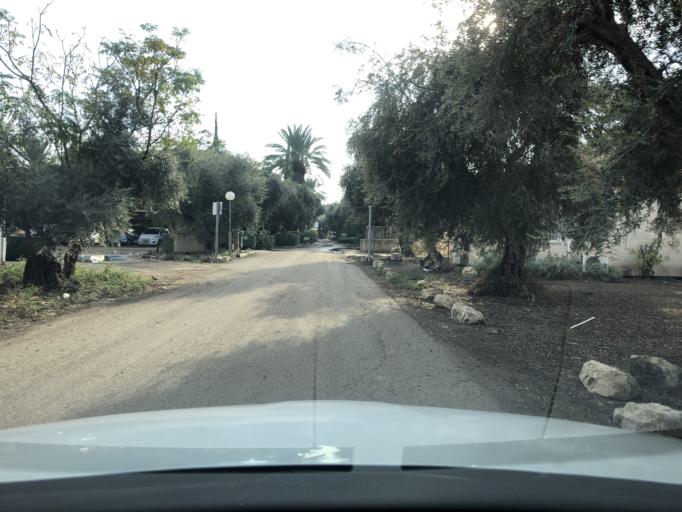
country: IL
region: Northern District
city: Yavne'el
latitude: 32.6586
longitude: 35.5832
